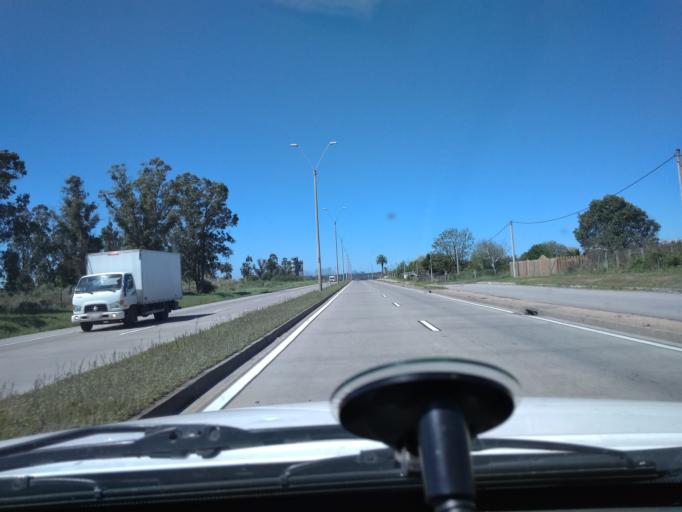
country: UY
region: Canelones
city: Toledo
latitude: -34.7950
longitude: -56.1279
